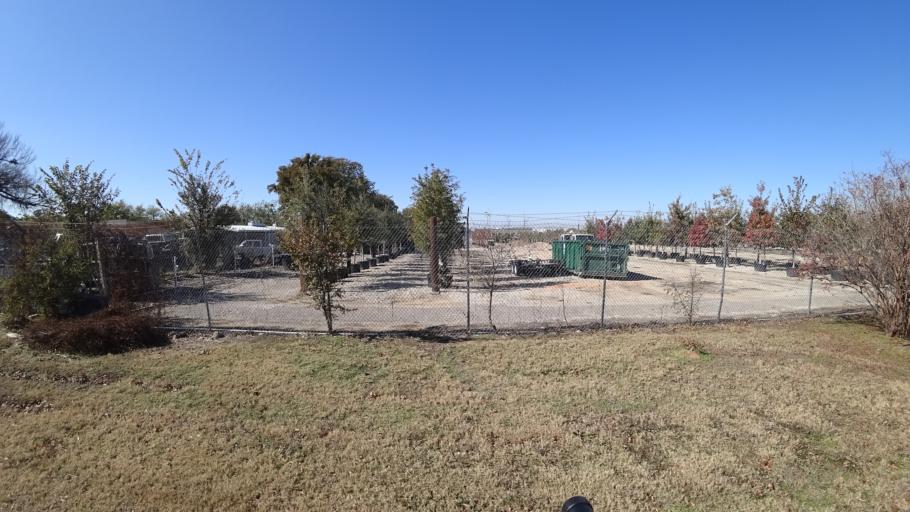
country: US
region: Texas
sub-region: Denton County
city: Lewisville
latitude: 33.0427
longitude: -96.9406
